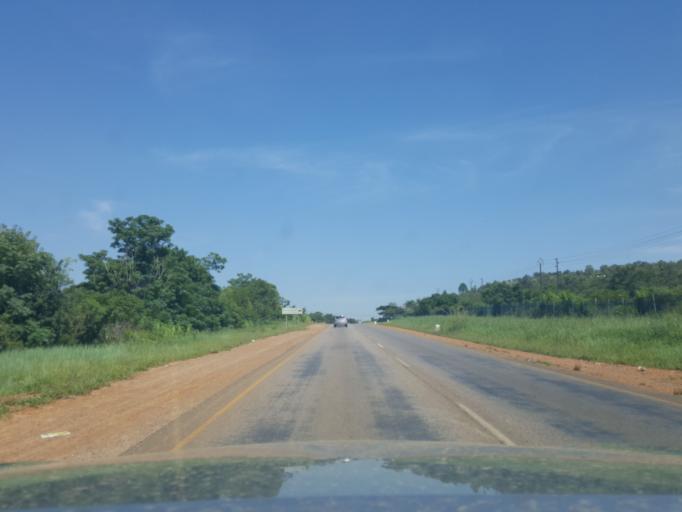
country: ZA
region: Gauteng
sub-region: City of Tshwane Metropolitan Municipality
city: Cullinan
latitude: -25.6783
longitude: 28.3541
